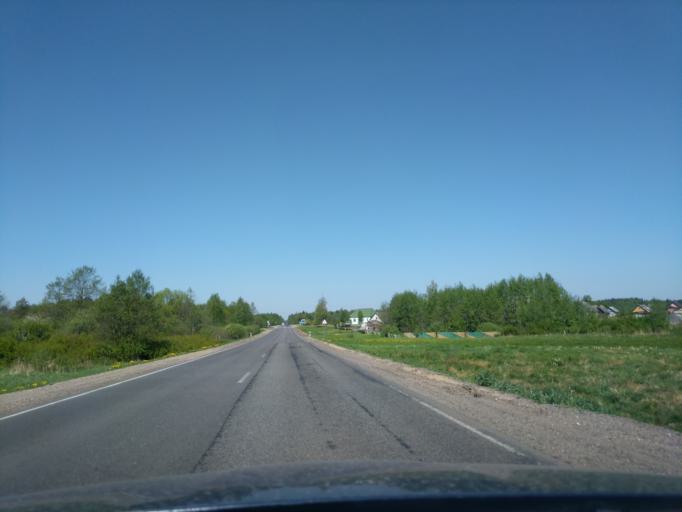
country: BY
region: Minsk
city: Il'ya
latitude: 54.3963
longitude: 27.3377
